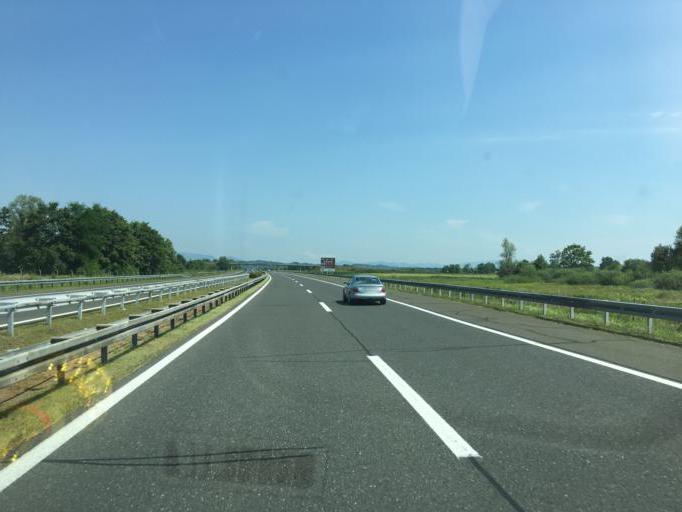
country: HR
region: Zagrebacka
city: Jakovlje
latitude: 45.9702
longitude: 15.8517
